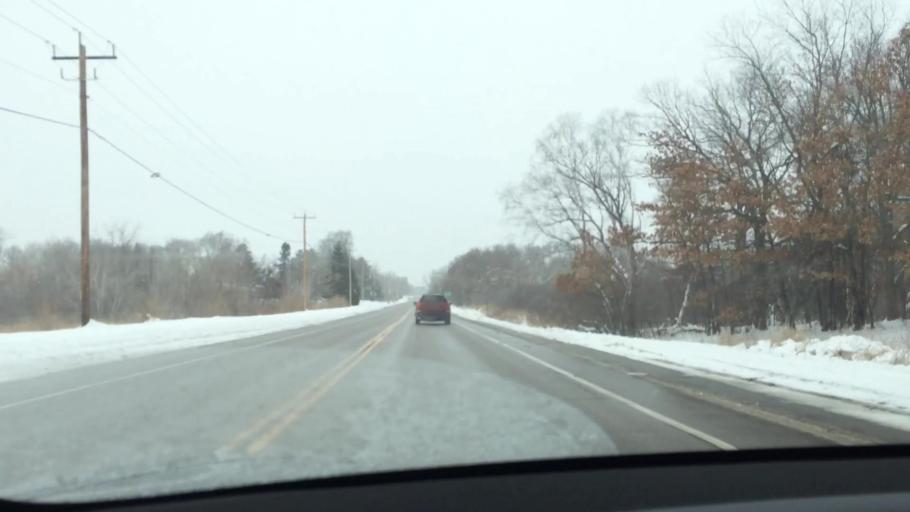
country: US
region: Minnesota
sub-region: Ramsey County
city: Shoreview
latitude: 45.1124
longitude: -93.1273
